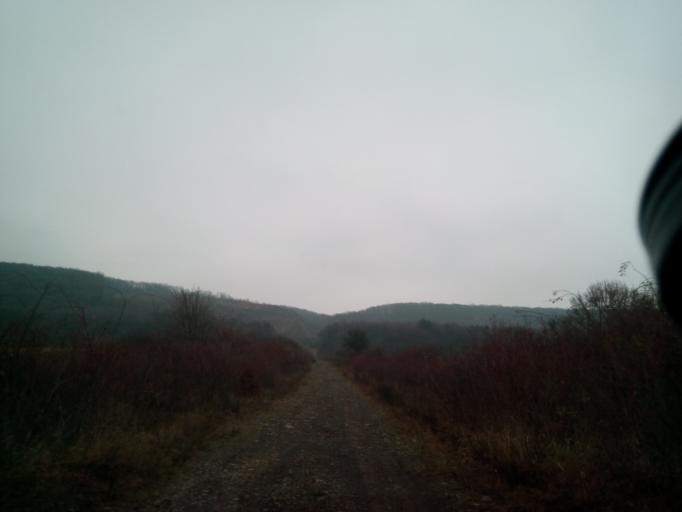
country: SK
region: Kosicky
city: Kosice
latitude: 48.6919
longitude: 21.4490
